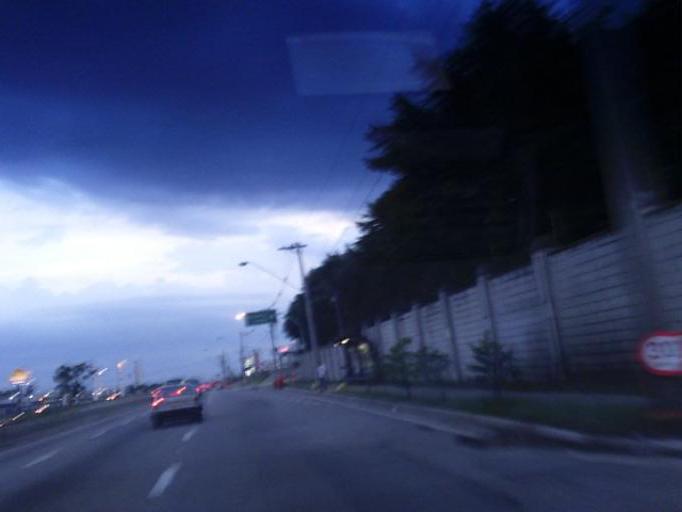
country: BR
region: Sao Paulo
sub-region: Sao Jose Dos Campos
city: Sao Jose dos Campos
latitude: -23.2251
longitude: -45.9064
